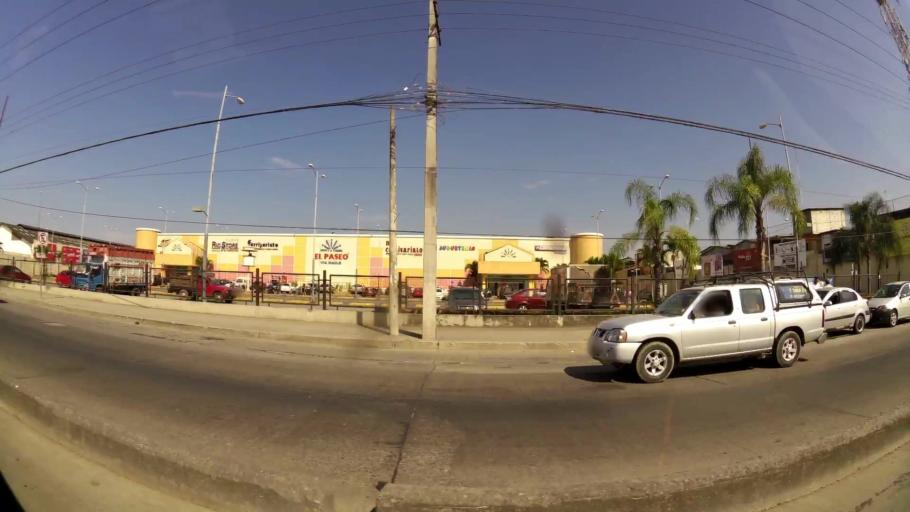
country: EC
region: Guayas
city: Guayaquil
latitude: -2.1146
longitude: -79.9330
